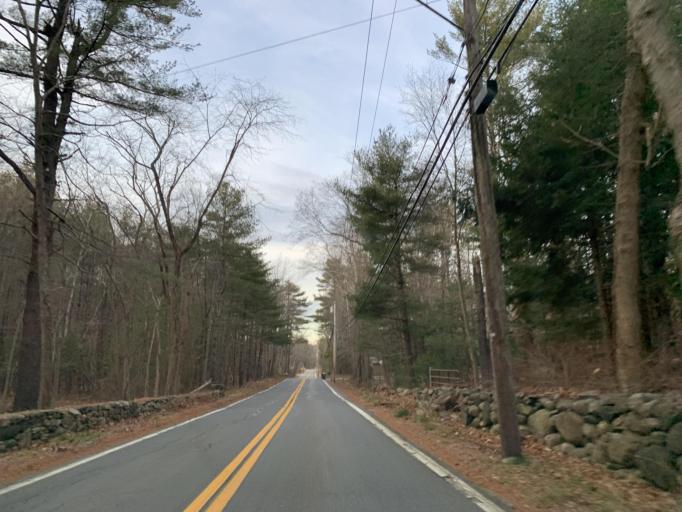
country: US
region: Rhode Island
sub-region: Providence County
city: Pascoag
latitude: 41.9317
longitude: -71.7007
